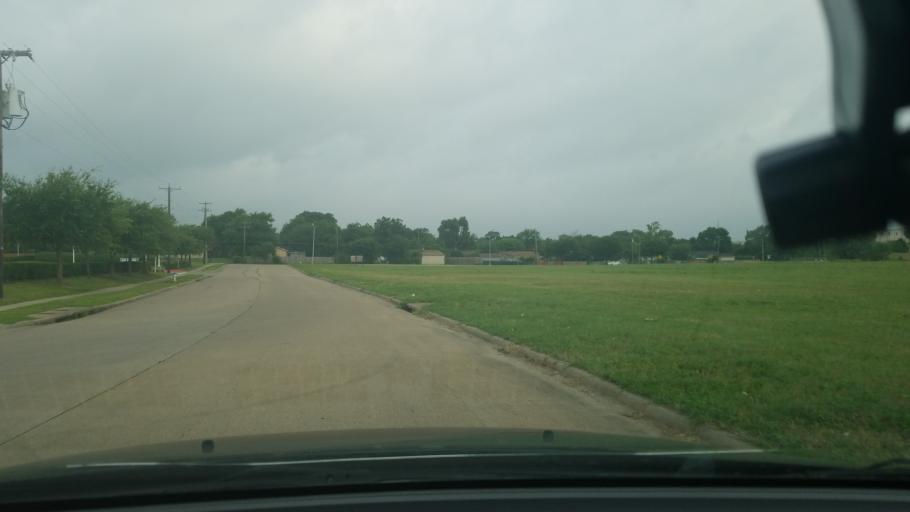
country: US
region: Texas
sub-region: Dallas County
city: Mesquite
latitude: 32.7712
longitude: -96.6270
